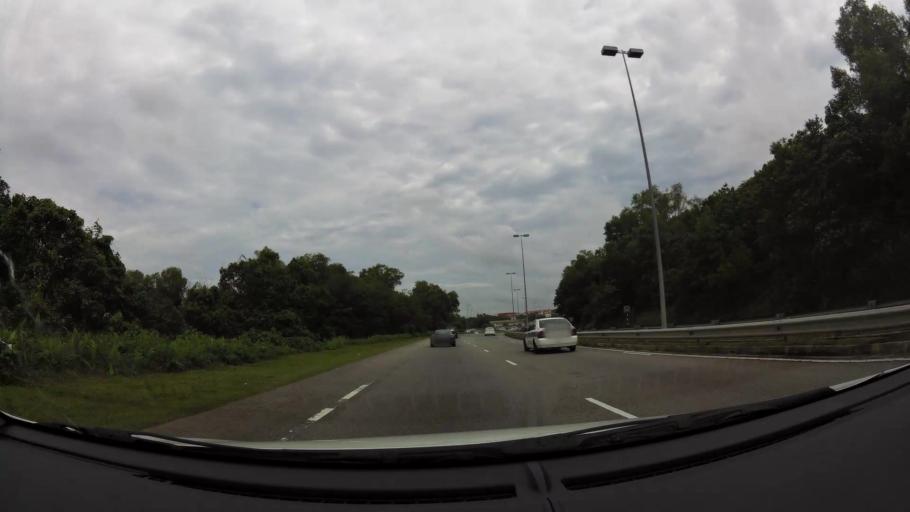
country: BN
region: Brunei and Muara
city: Bandar Seri Begawan
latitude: 4.9110
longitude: 114.9074
